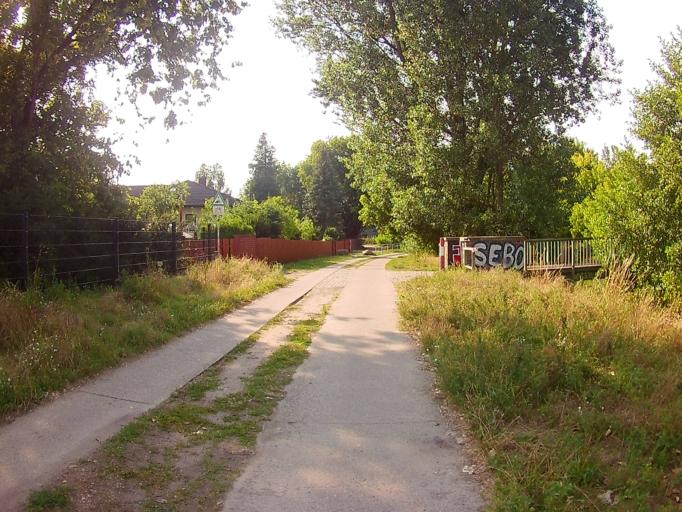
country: DE
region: Berlin
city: Biesdorf
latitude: 52.4783
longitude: 13.5642
